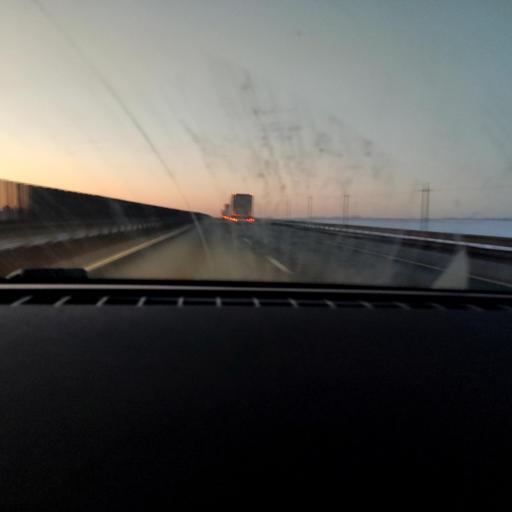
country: RU
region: Samara
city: Mirnyy
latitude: 53.4600
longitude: 50.2116
